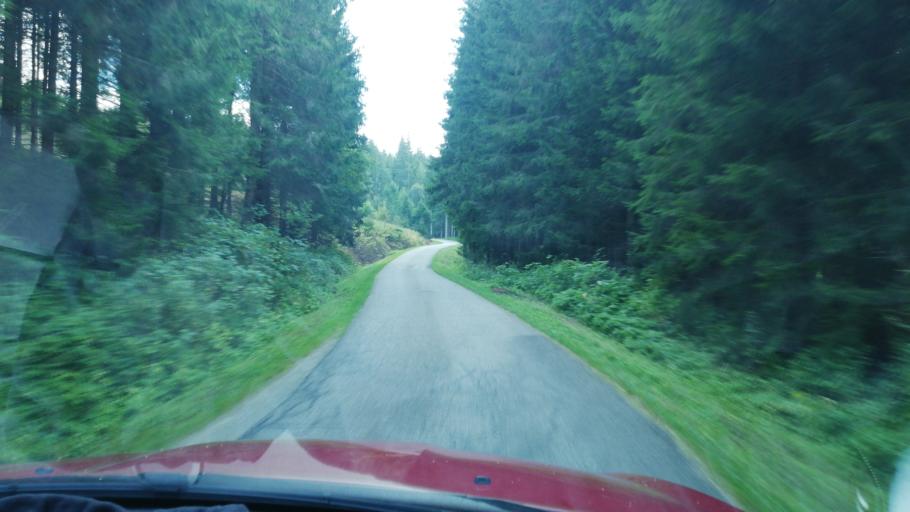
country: AT
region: Lower Austria
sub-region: Politischer Bezirk Zwettl
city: Langschlag
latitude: 48.4880
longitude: 14.8408
